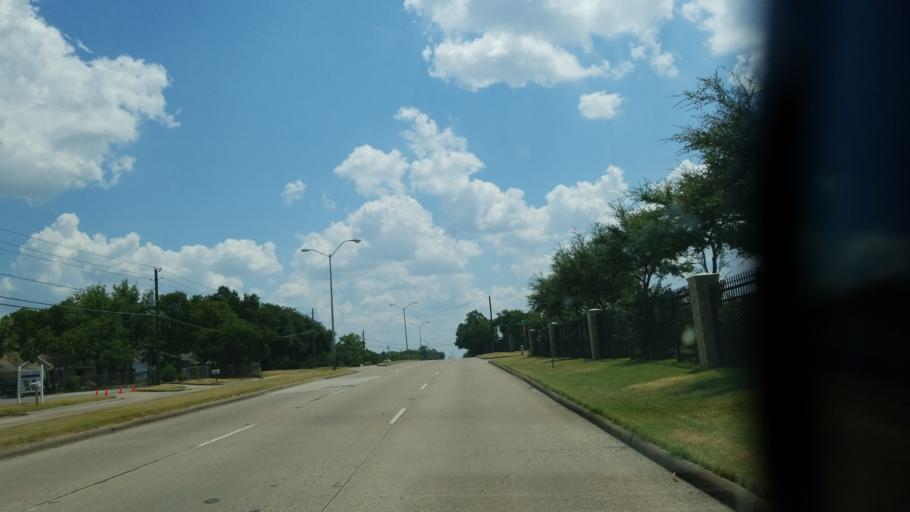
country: US
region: Texas
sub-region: Dallas County
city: Duncanville
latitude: 32.6748
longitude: -96.8915
